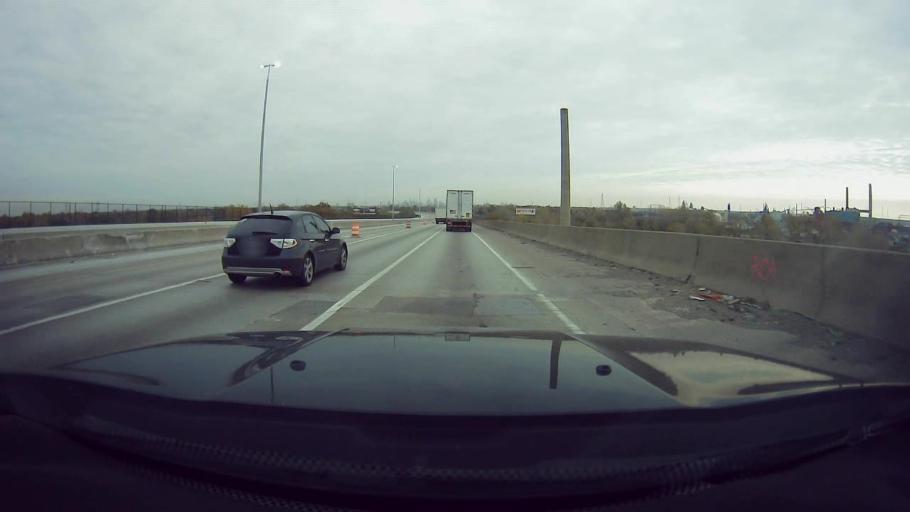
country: US
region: Michigan
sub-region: Wayne County
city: River Rouge
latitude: 42.2883
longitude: -83.1358
